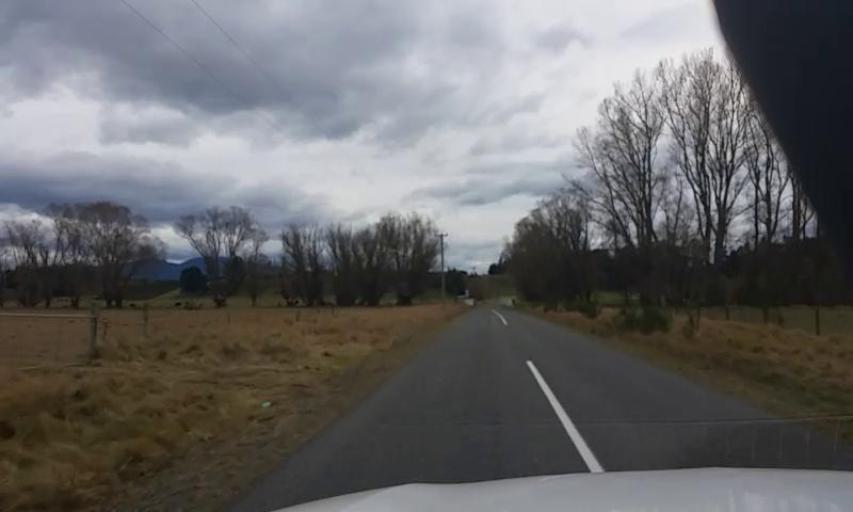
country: NZ
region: Canterbury
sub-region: Waimakariri District
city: Kaiapoi
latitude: -43.3035
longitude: 172.4379
